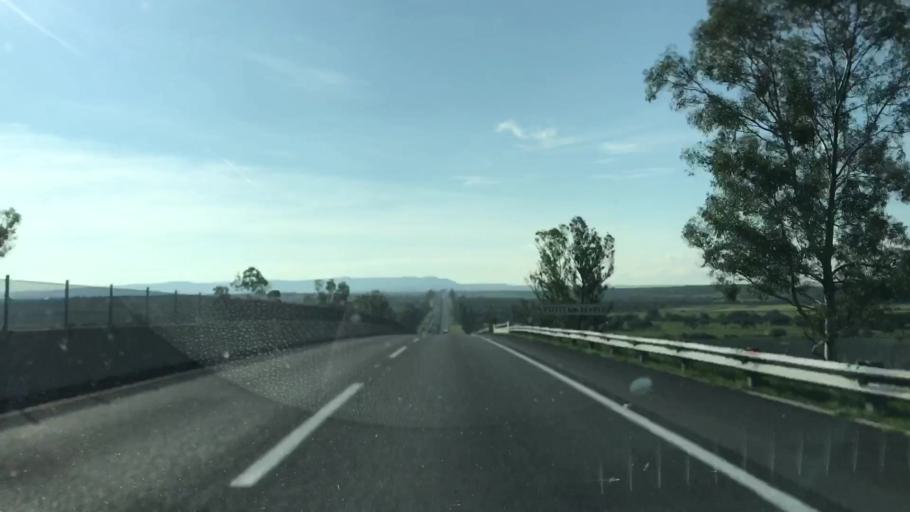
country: MX
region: Jalisco
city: Encarnacion de Diaz
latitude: 21.4775
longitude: -102.2301
